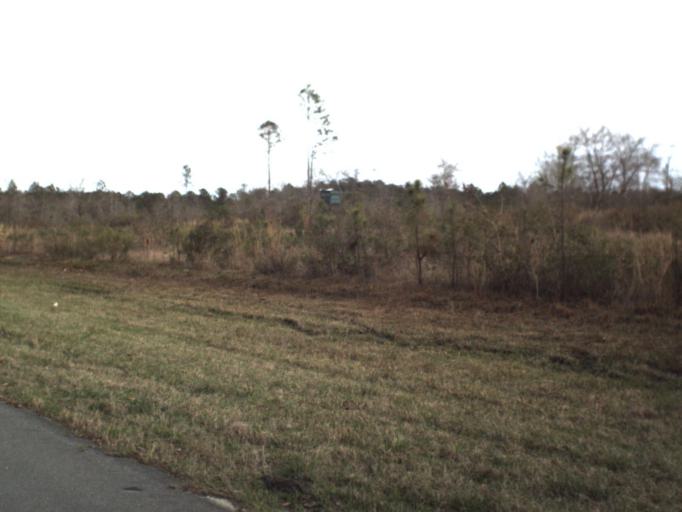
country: US
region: Florida
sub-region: Bay County
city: Callaway
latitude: 30.1415
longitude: -85.4118
